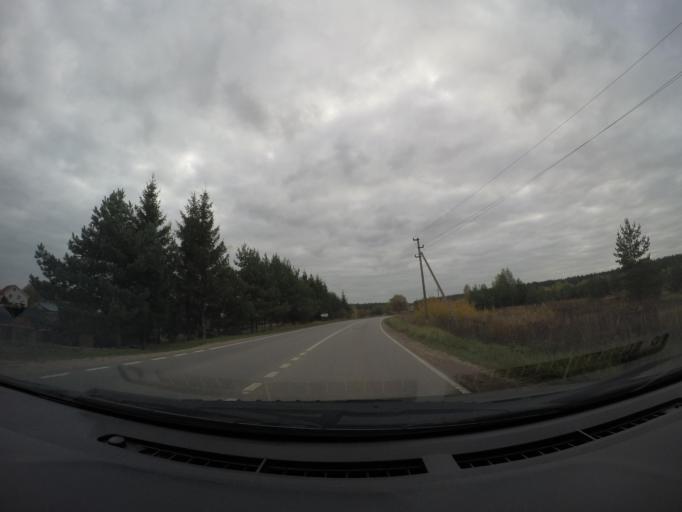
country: RU
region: Moskovskaya
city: Gzhel'
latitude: 55.6425
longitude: 38.4104
